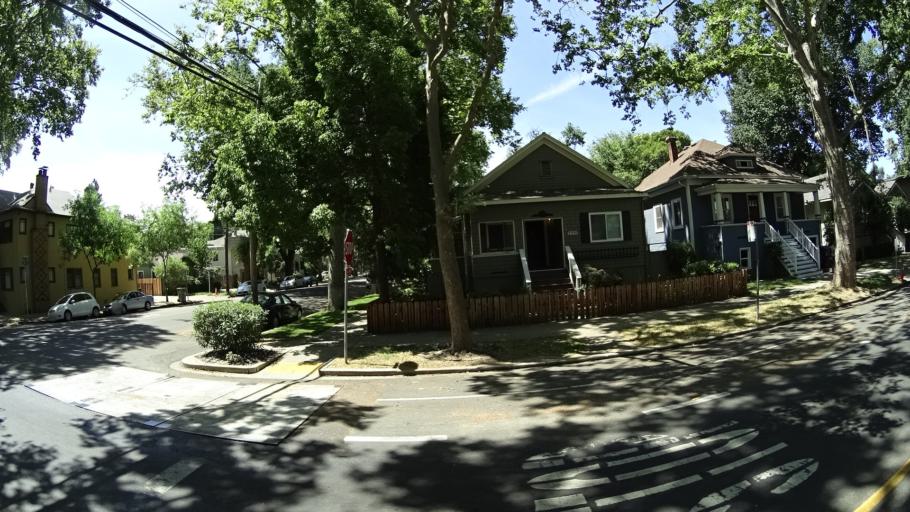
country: US
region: California
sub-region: Sacramento County
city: Sacramento
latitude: 38.5797
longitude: -121.4728
